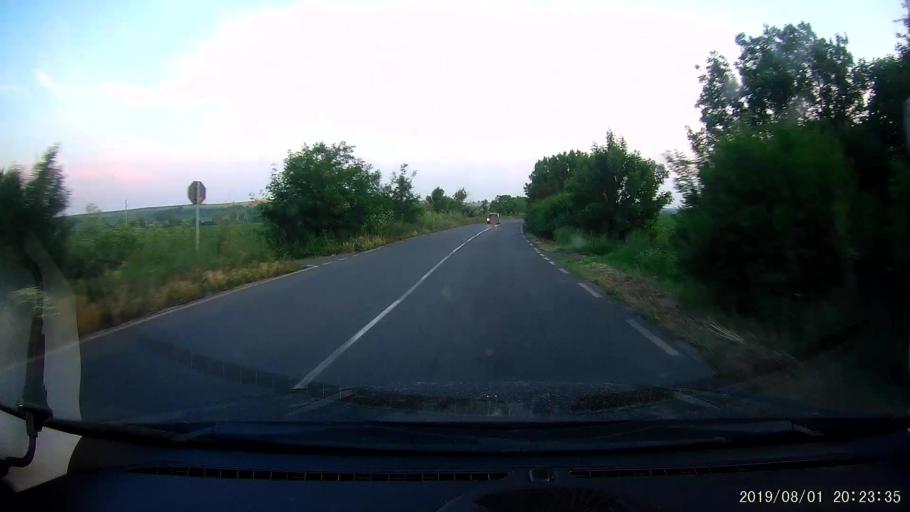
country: BG
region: Yambol
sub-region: Obshtina Elkhovo
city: Elkhovo
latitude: 42.2458
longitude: 26.5989
